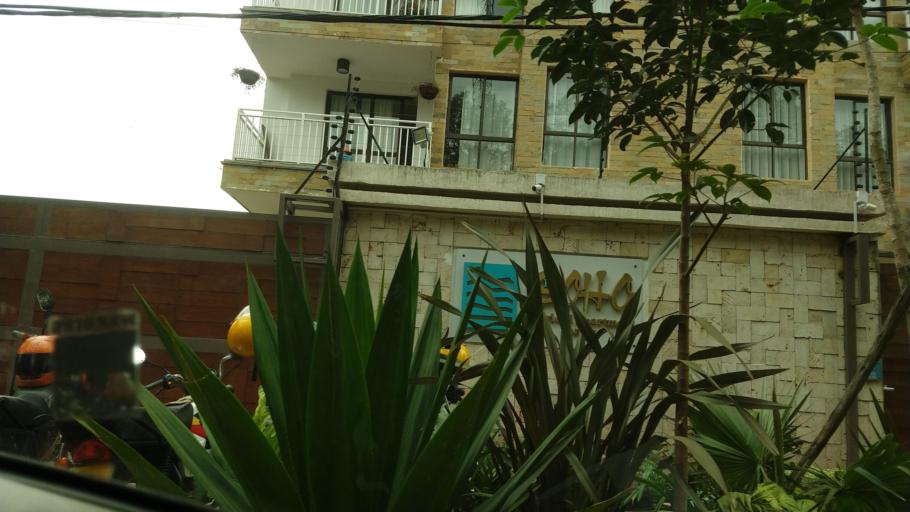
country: KE
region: Nairobi Area
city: Nairobi
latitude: -1.2904
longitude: 36.7816
